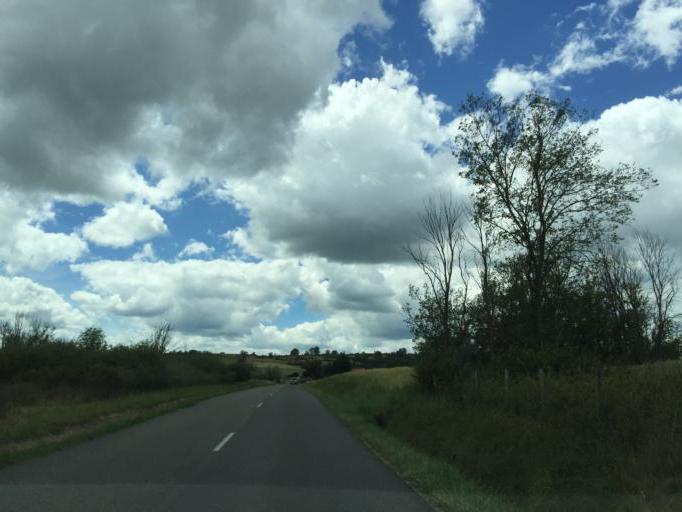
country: FR
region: Rhone-Alpes
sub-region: Departement de la Loire
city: Saint-Marcellin-en-Forez
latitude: 45.5005
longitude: 4.1538
